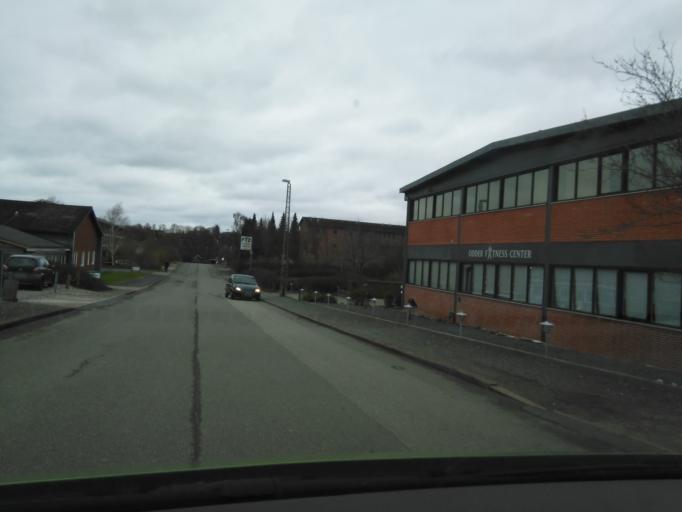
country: DK
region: Central Jutland
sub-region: Odder Kommune
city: Odder
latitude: 55.9831
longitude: 10.1490
